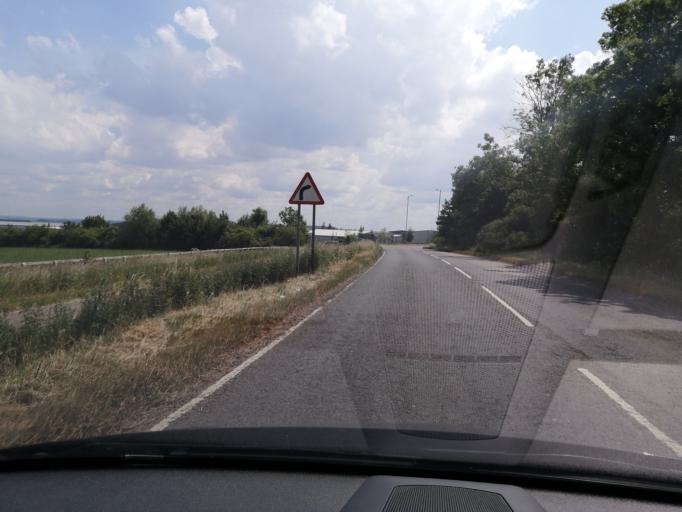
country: GB
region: England
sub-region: Cambridgeshire
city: Yaxley
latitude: 52.5287
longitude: -0.2382
